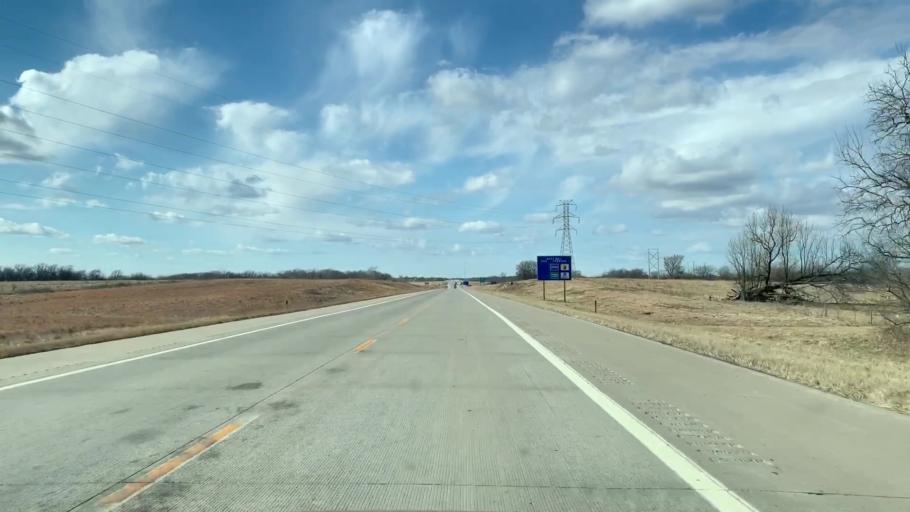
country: US
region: Kansas
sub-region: Labette County
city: Parsons
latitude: 37.3639
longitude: -95.2402
